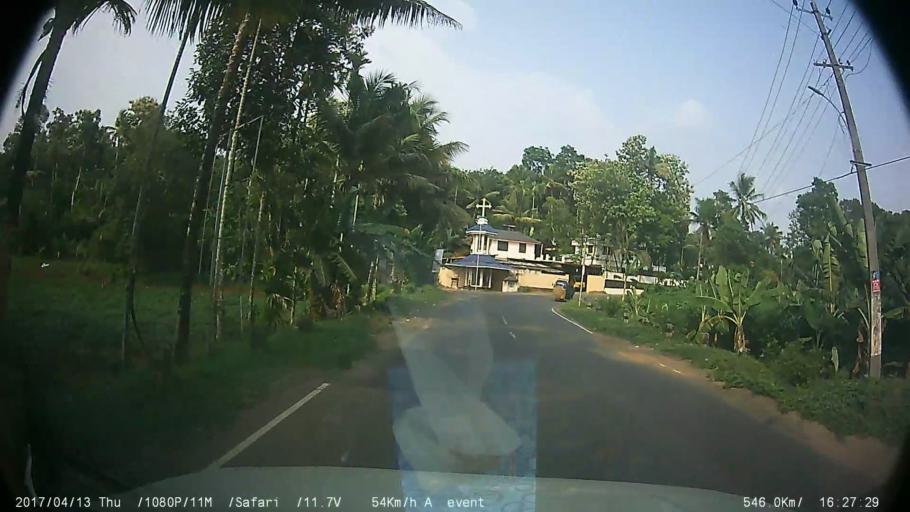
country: IN
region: Kerala
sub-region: Ernakulam
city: Piravam
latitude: 9.8342
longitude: 76.5171
